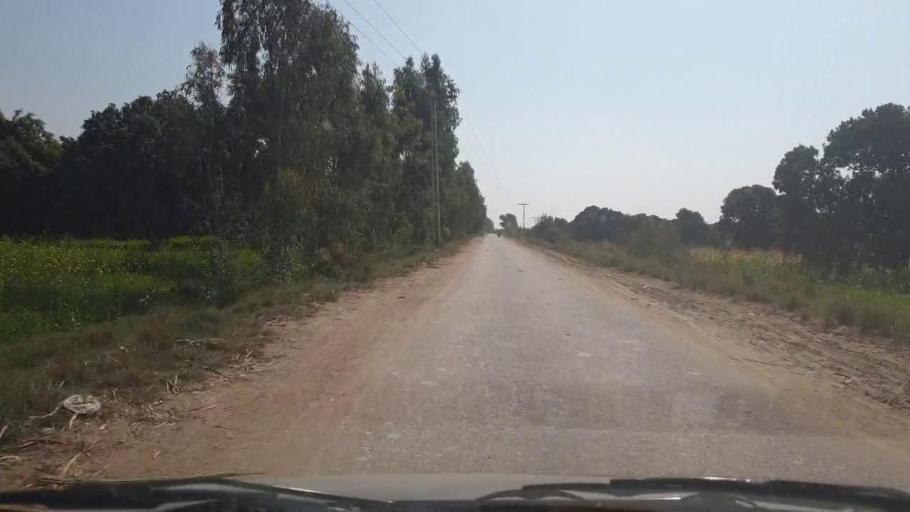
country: PK
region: Sindh
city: Samaro
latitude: 25.2675
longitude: 69.3477
